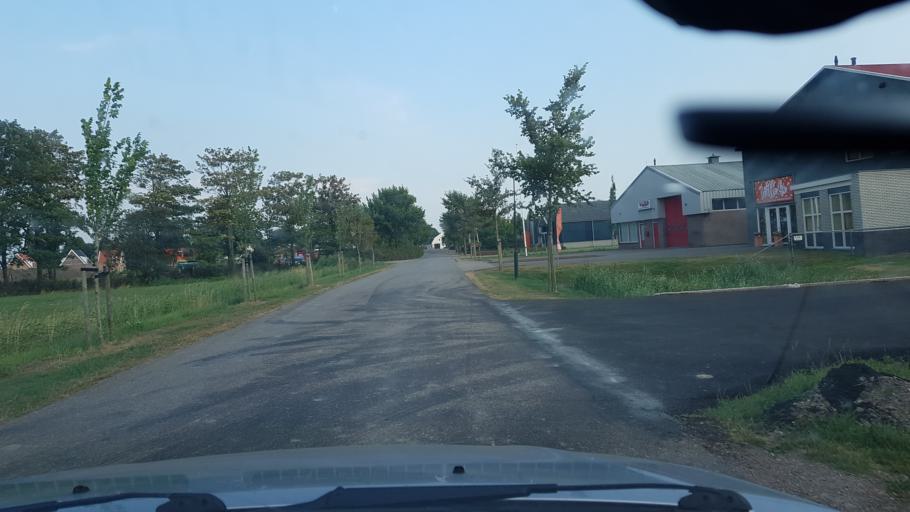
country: NL
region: Friesland
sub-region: Gemeente Ferwerderadiel
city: Burdaard
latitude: 53.2981
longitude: 5.8773
